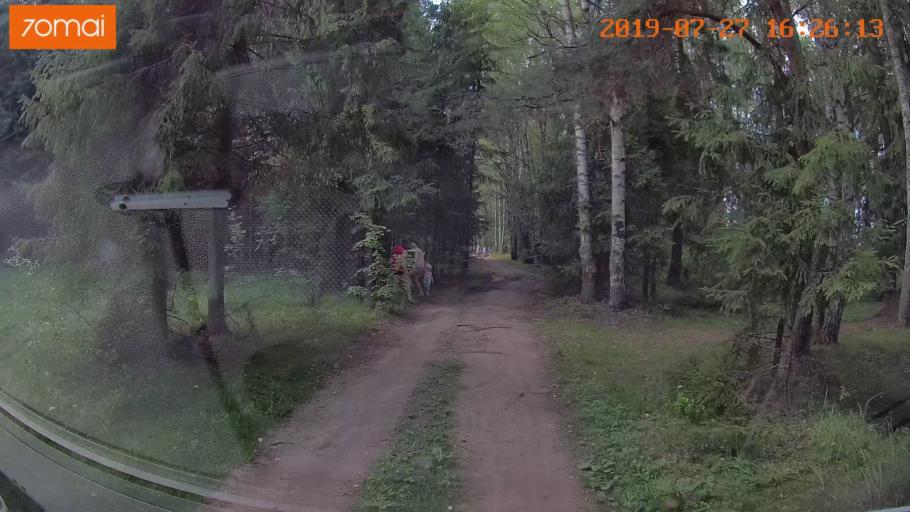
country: RU
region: Ivanovo
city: Novo-Talitsy
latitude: 57.0910
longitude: 40.8545
